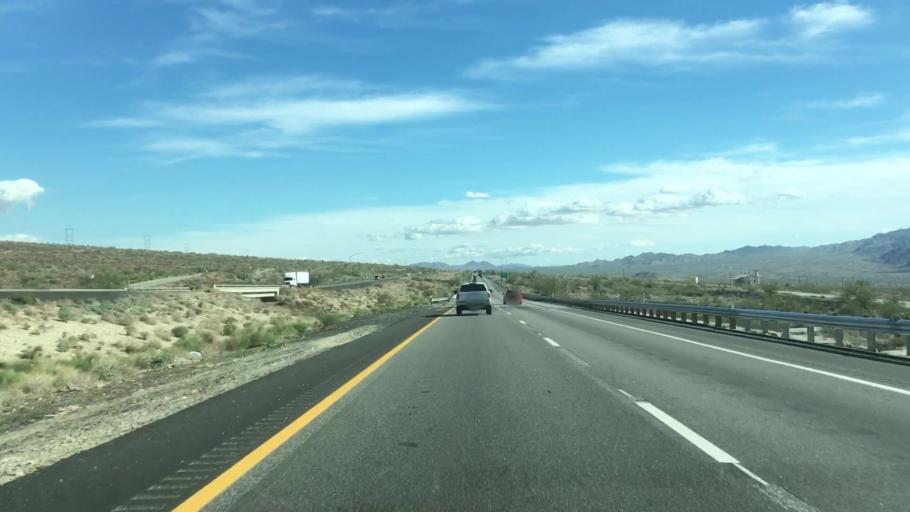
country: US
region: California
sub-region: Riverside County
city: Mecca
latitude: 33.6705
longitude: -115.9191
